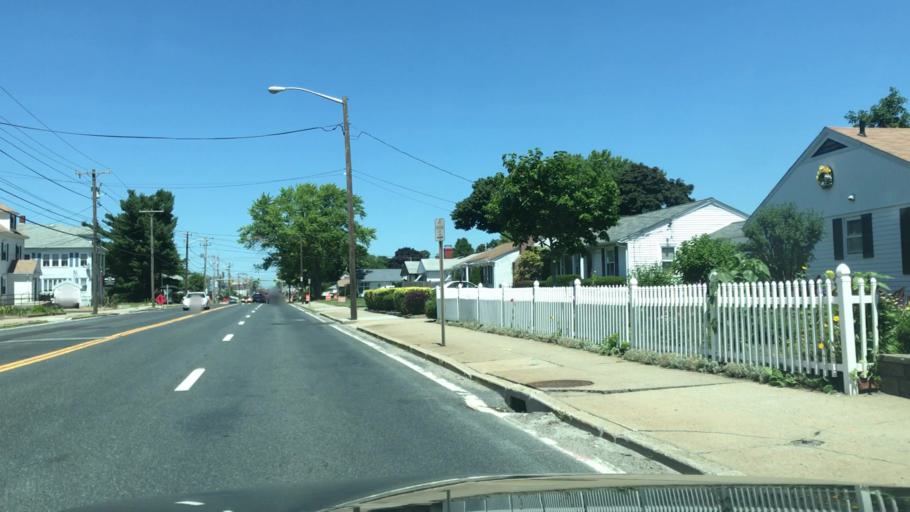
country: US
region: Rhode Island
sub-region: Providence County
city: Pawtucket
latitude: 41.8733
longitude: -71.3543
